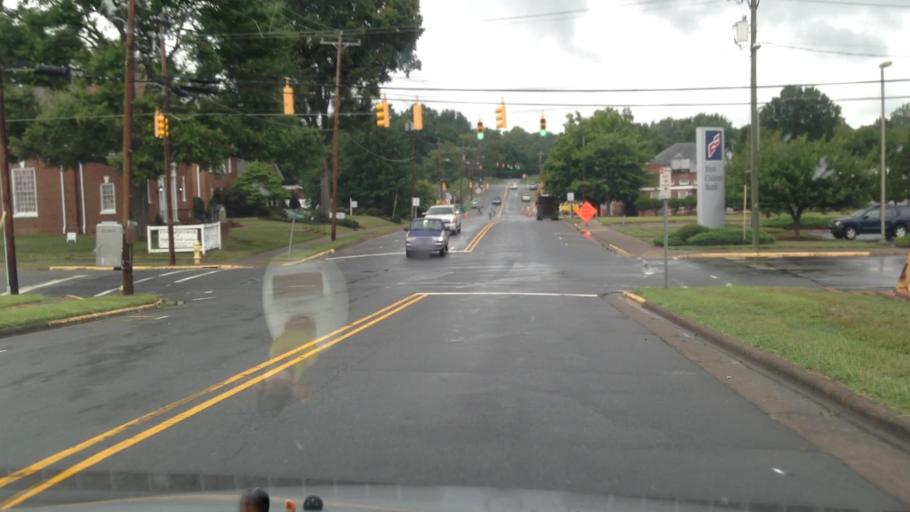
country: US
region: North Carolina
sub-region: Rockingham County
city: Madison
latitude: 36.3861
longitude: -79.9616
